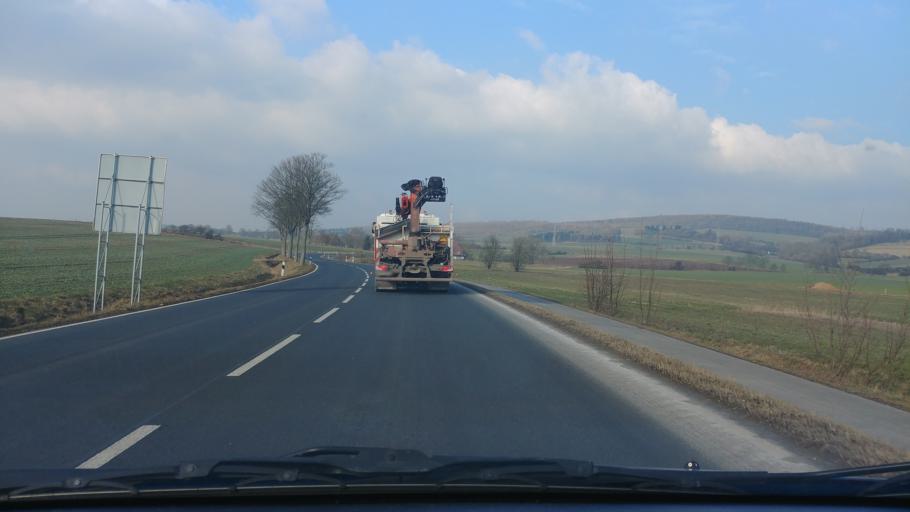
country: DE
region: Lower Saxony
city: Freden
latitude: 51.8840
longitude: 9.8819
